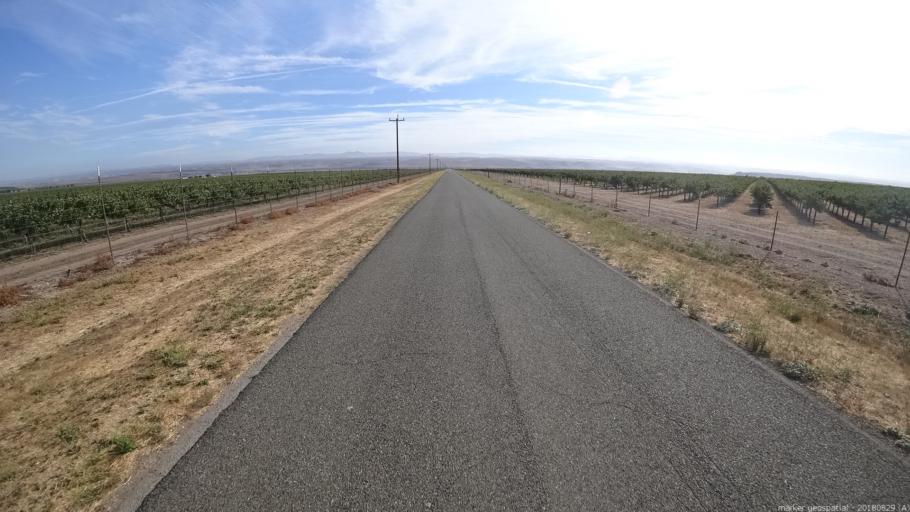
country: US
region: California
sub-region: Monterey County
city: King City
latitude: 36.0850
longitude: -121.0348
